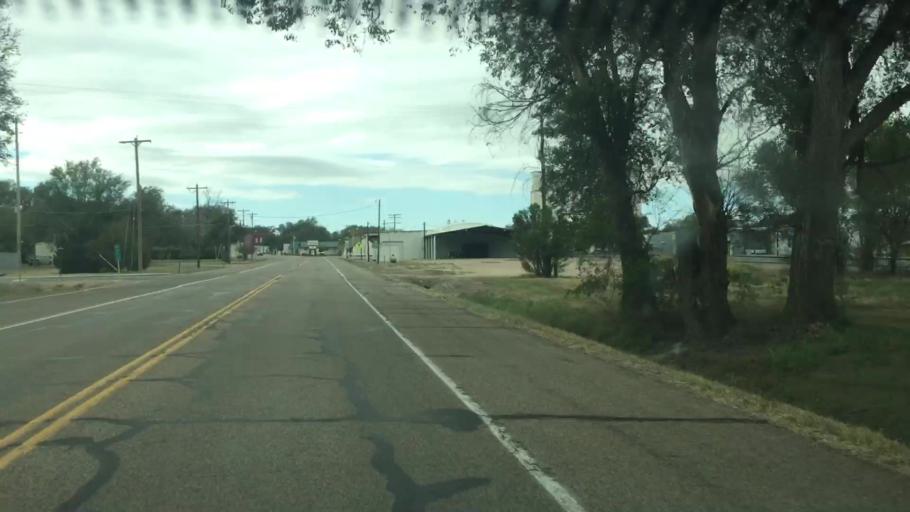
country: US
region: Colorado
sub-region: Prowers County
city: Lamar
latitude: 38.0623
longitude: -102.3057
